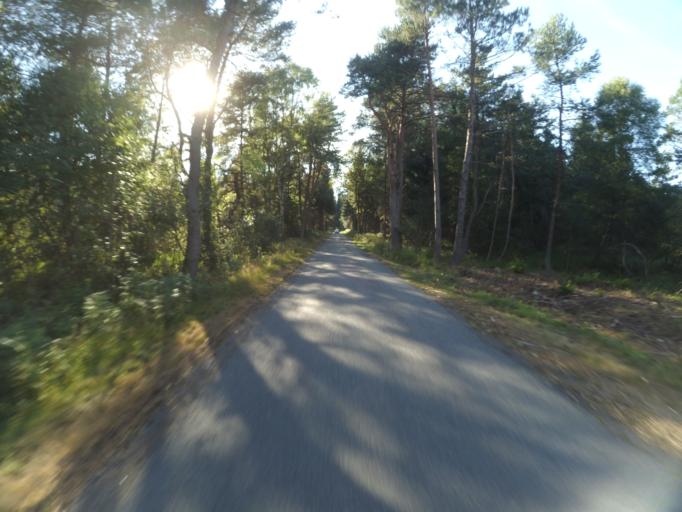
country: FR
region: Limousin
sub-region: Departement de la Creuse
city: Banize
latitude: 45.7905
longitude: 1.9548
